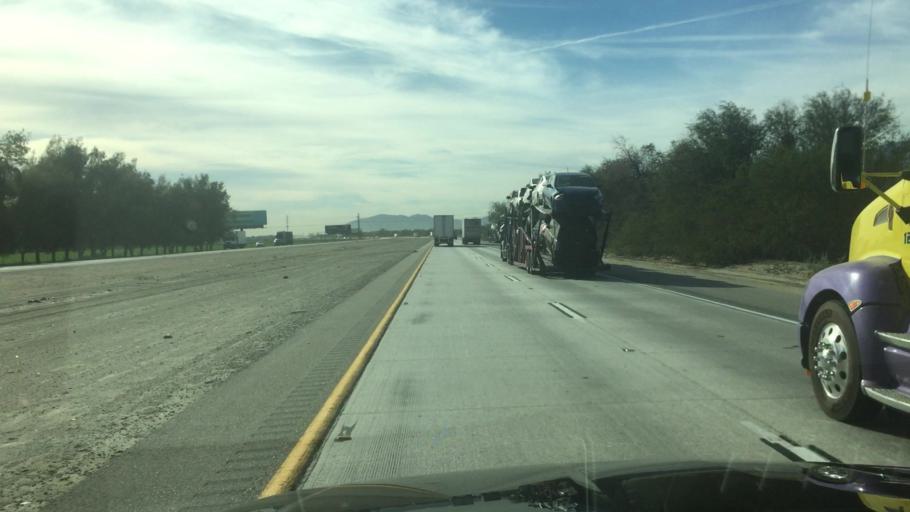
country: US
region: California
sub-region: Riverside County
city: Thermal
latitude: 33.6626
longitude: -116.1424
